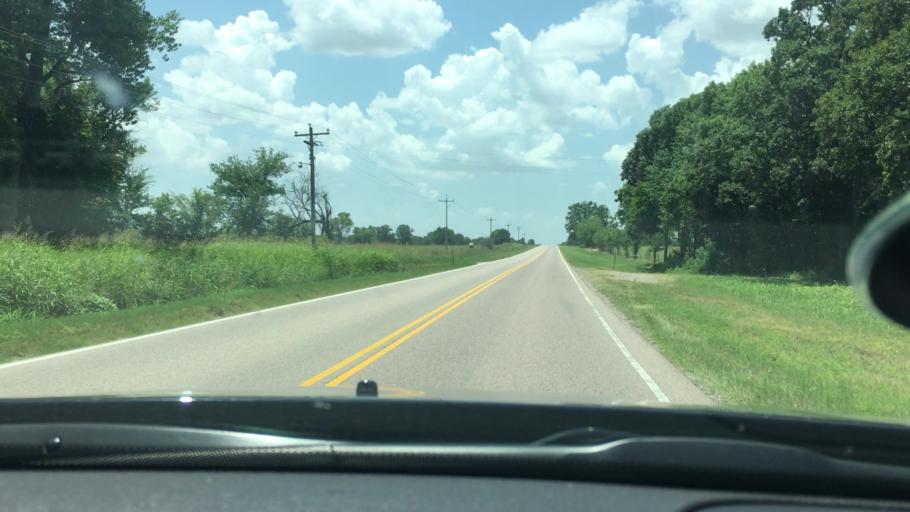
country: US
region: Oklahoma
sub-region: Johnston County
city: Tishomingo
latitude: 34.4820
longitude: -96.6278
